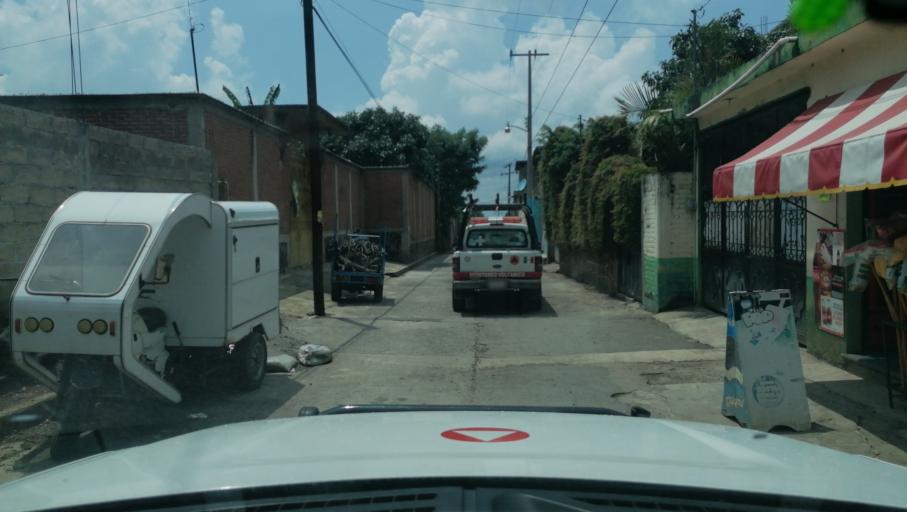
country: MX
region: Morelos
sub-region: Yecapixtla
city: Yecapixtla
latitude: 18.8826
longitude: -98.8204
